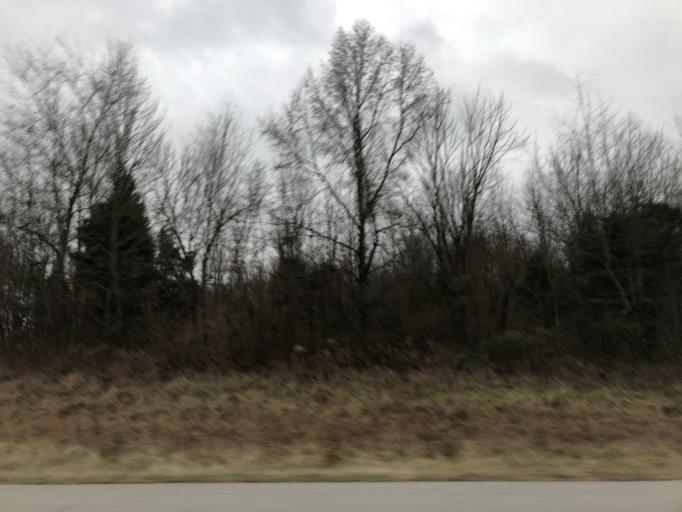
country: US
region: Illinois
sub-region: Johnson County
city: Vienna
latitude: 37.3626
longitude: -88.7993
